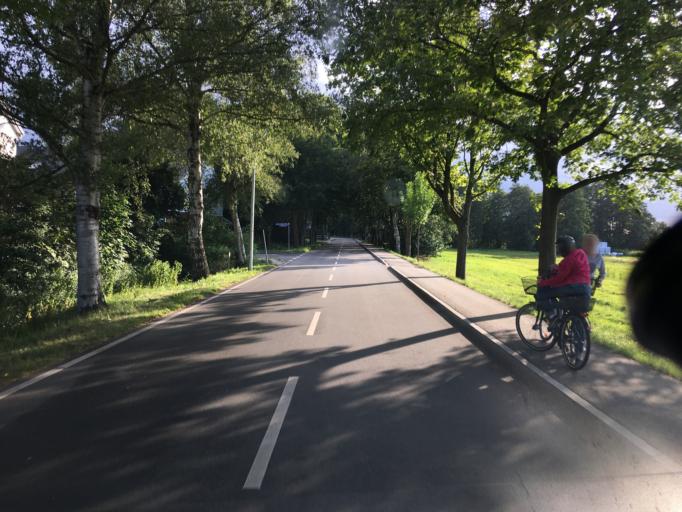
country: DE
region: Lower Saxony
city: Neu Wulmstorf
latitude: 53.4850
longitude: 9.8651
